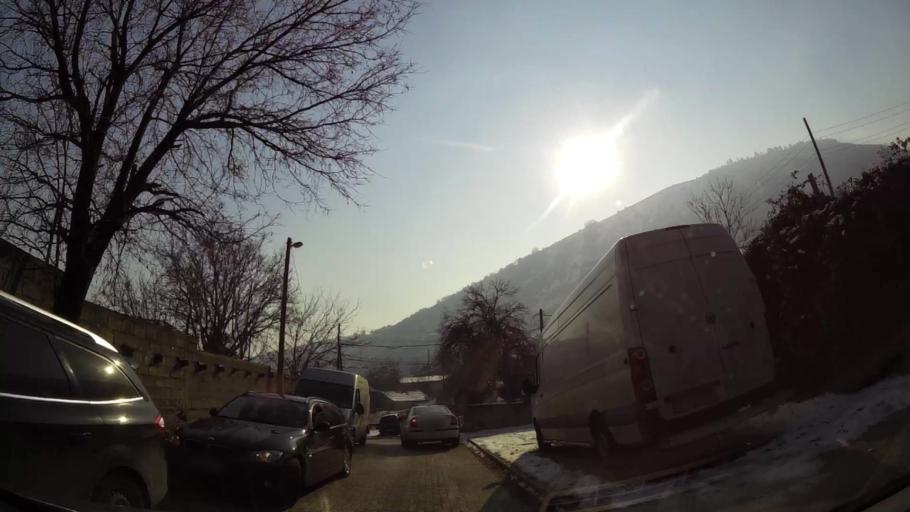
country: MK
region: Sopiste
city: Sopishte
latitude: 41.9737
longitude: 21.4366
